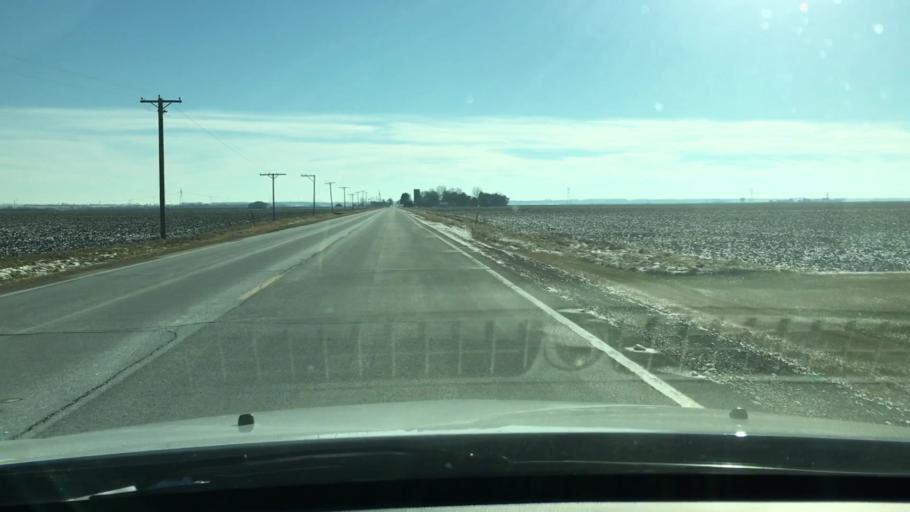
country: US
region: Illinois
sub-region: Ogle County
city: Rochelle
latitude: 41.8142
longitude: -89.0833
